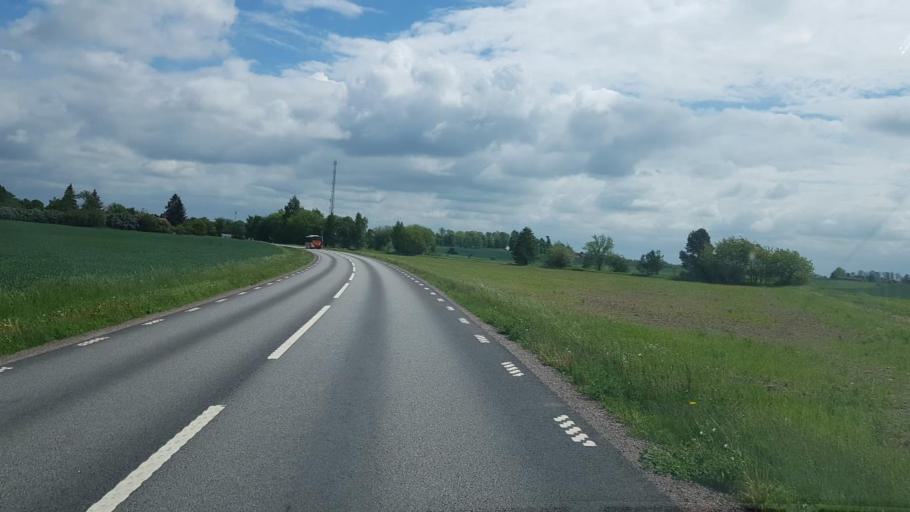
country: SE
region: OEstergoetland
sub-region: Motala Kommun
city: Borensberg
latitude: 58.4801
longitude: 15.2182
